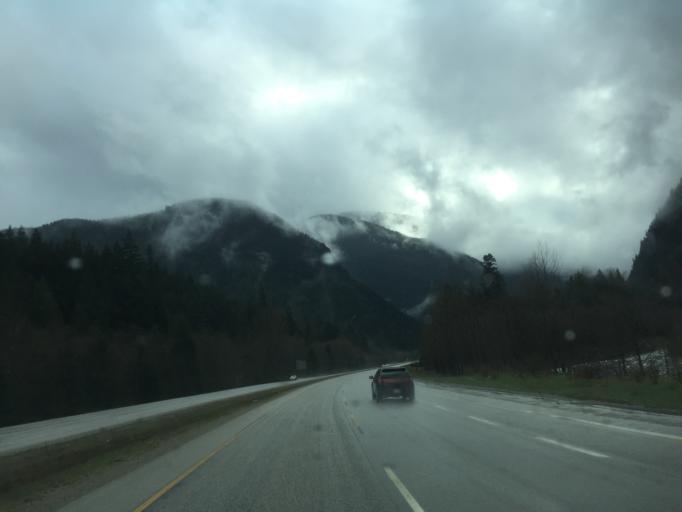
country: CA
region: British Columbia
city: Hope
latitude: 49.4632
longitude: -121.2547
